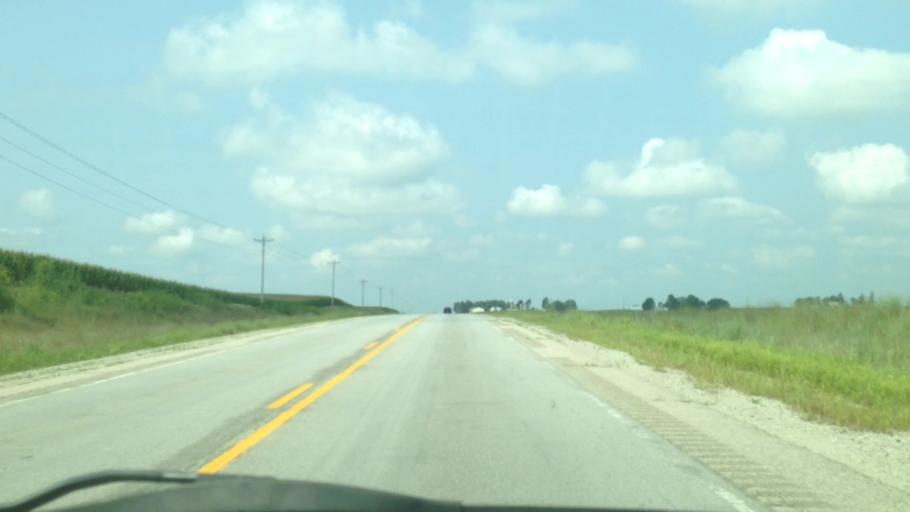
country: US
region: Iowa
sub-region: Benton County
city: Walford
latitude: 41.8762
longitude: -91.8557
